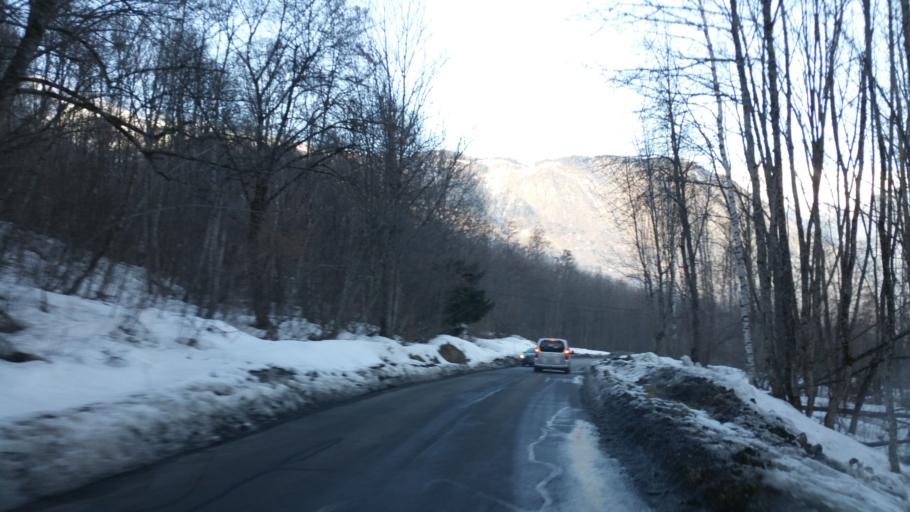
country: FR
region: Rhone-Alpes
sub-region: Departement de la Savoie
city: Saint-Jean-de-Maurienne
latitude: 45.2671
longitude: 6.3118
